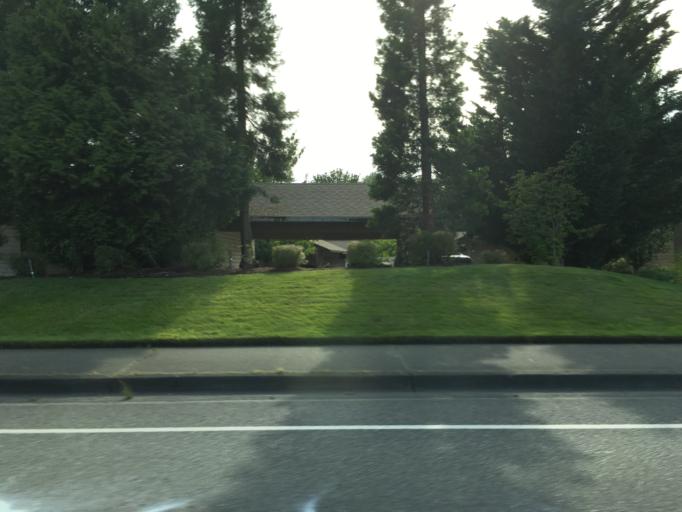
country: US
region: Washington
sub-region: Snohomish County
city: North Creek
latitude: 47.8250
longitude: -122.2076
